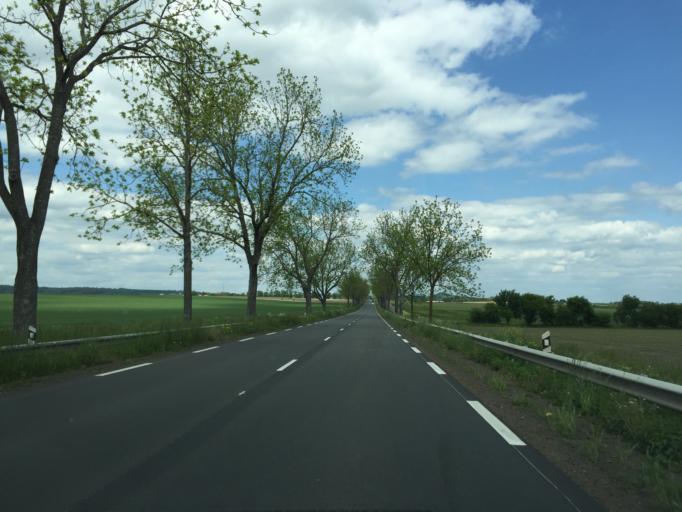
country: FR
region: Auvergne
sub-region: Departement du Puy-de-Dome
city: Aigueperse
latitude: 45.9984
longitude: 3.1917
